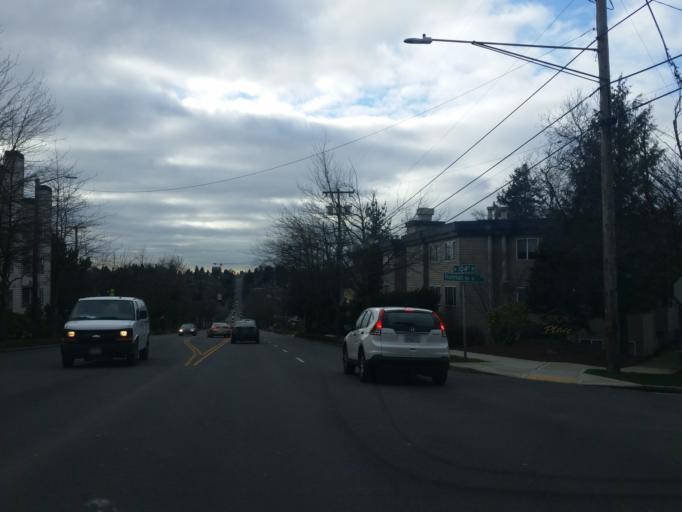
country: US
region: Washington
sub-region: King County
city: Shoreline
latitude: 47.7043
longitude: -122.3571
